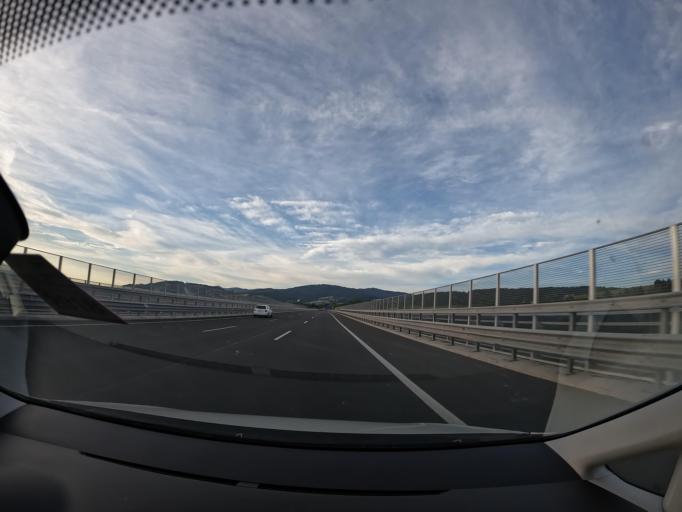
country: AT
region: Carinthia
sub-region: Politischer Bezirk Wolfsberg
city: Bad Sankt Leonhard im Lavanttal
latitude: 46.9276
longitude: 14.8212
